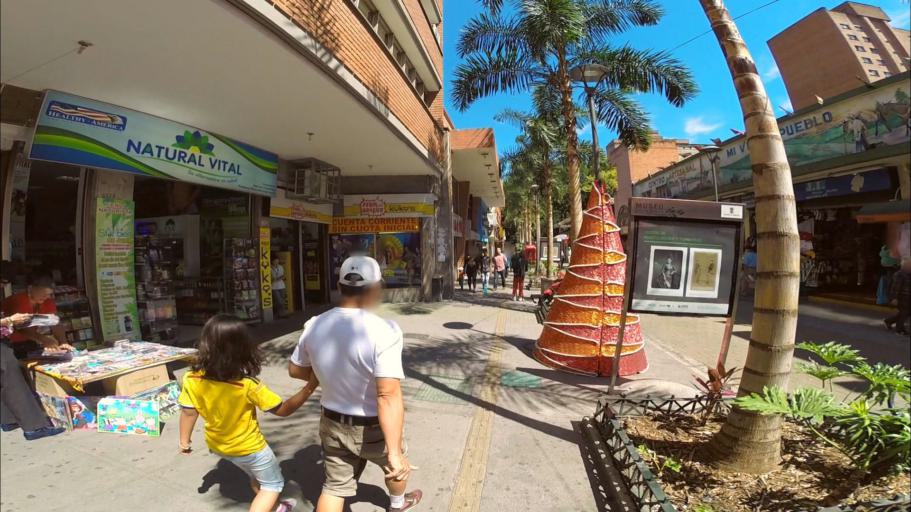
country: CO
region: Antioquia
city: Medellin
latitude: 6.2517
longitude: -75.5653
